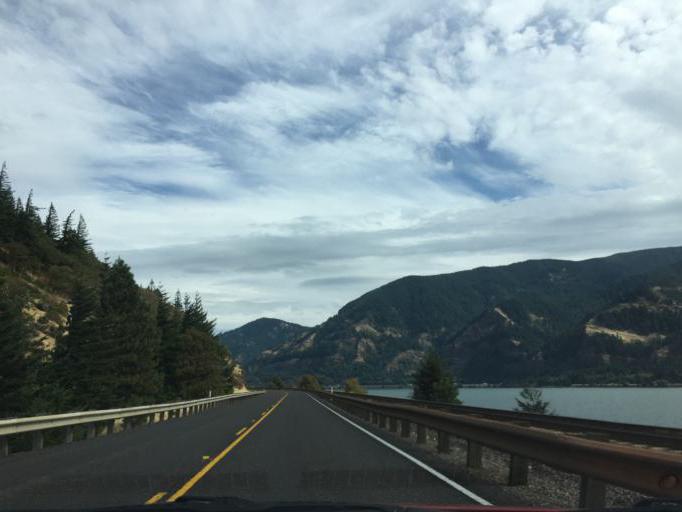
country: US
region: Washington
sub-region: Skamania County
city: Carson
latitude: 45.6991
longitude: -121.7201
